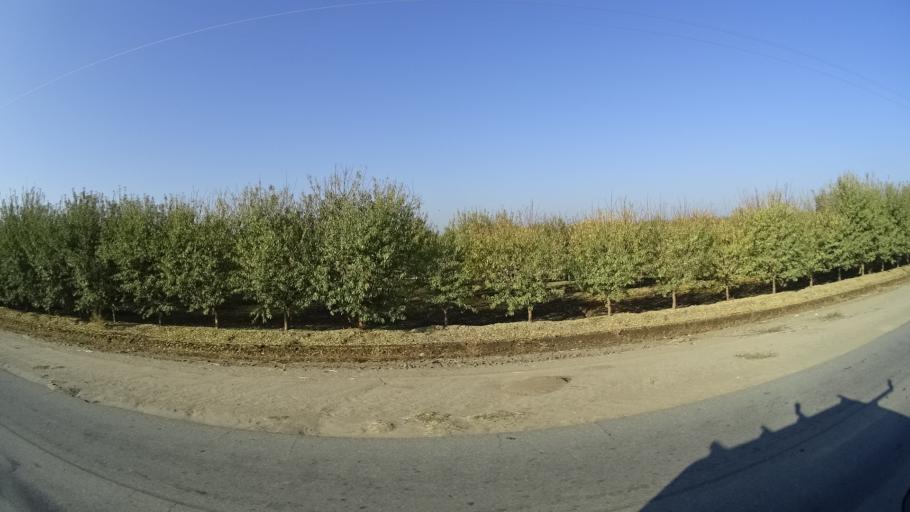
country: US
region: California
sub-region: Kern County
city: Greenfield
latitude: 35.2465
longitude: -118.9854
